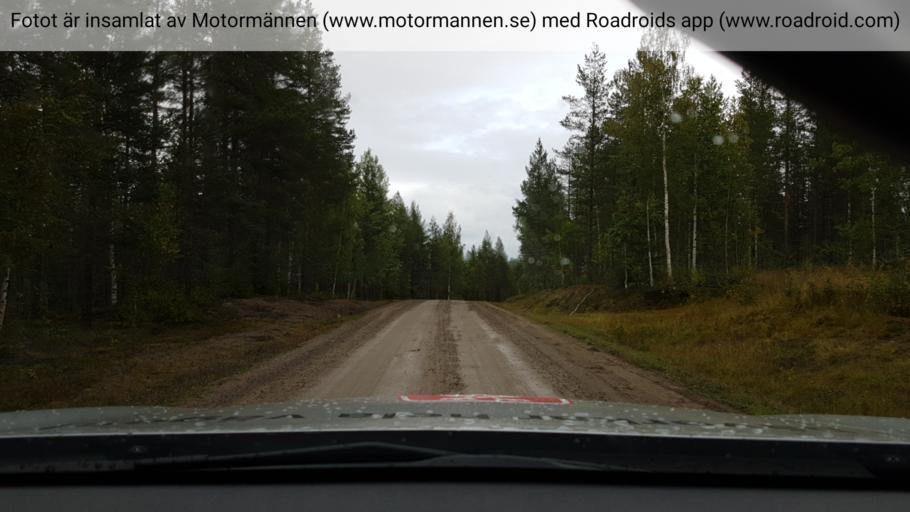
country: SE
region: Vaesterbotten
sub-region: Norsjo Kommun
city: Norsjoe
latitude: 65.2276
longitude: 19.8575
